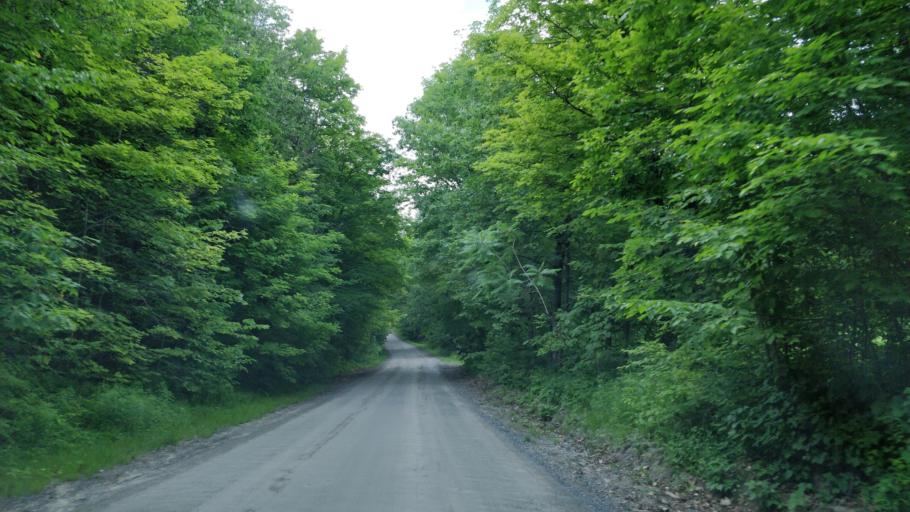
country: CA
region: Ontario
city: Perth
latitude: 44.6610
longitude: -76.5784
